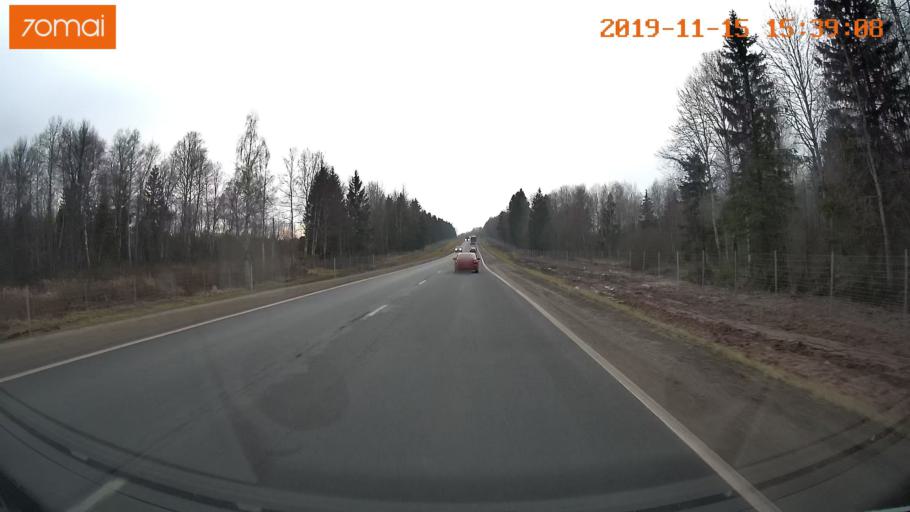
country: RU
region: Jaroslavl
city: Danilov
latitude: 58.0235
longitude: 40.0723
